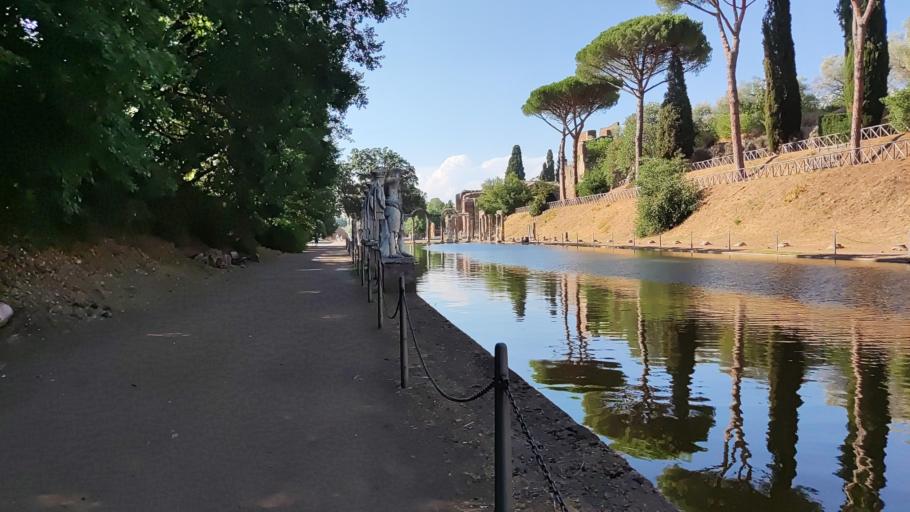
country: IT
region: Latium
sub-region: Citta metropolitana di Roma Capitale
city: Villa Adriana
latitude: 41.9382
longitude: 12.7760
